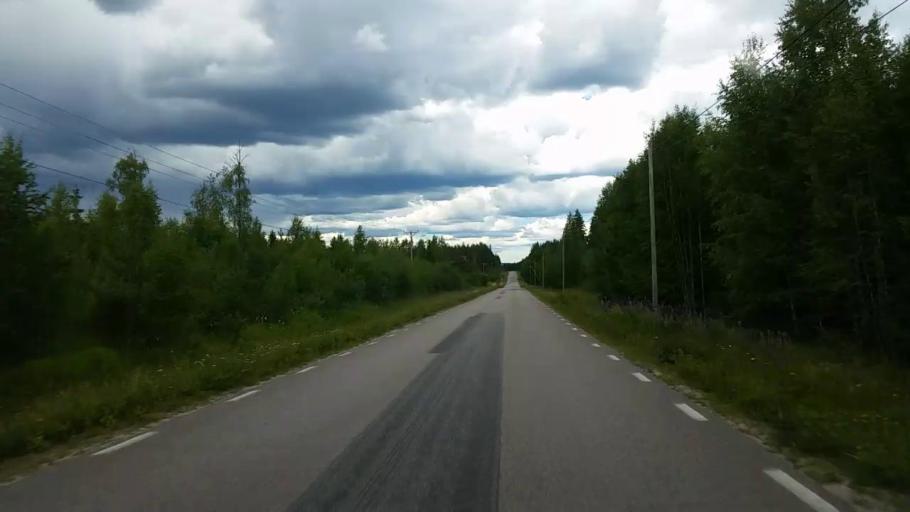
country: SE
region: Gaevleborg
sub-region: Ovanakers Kommun
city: Edsbyn
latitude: 61.4216
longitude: 15.8999
